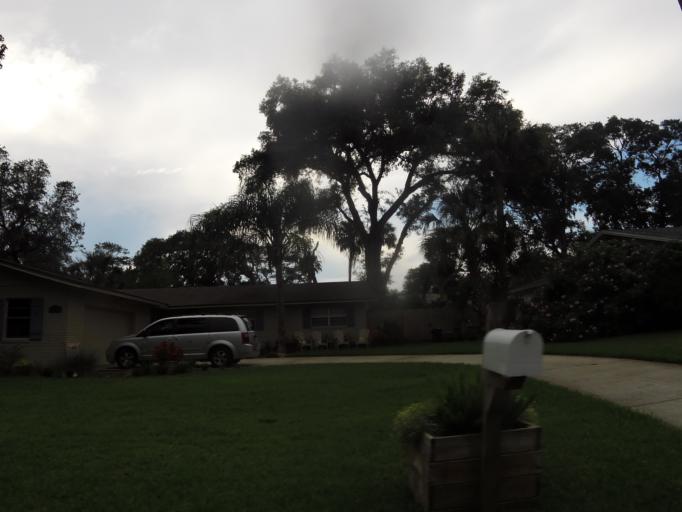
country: US
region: Florida
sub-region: Duval County
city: Jacksonville Beach
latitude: 30.2709
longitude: -81.4041
